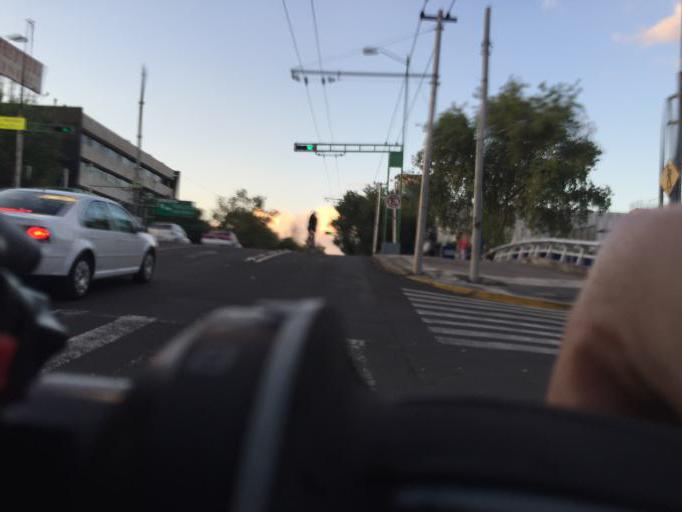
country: MX
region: Mexico City
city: Benito Juarez
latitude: 19.4036
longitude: -99.1450
